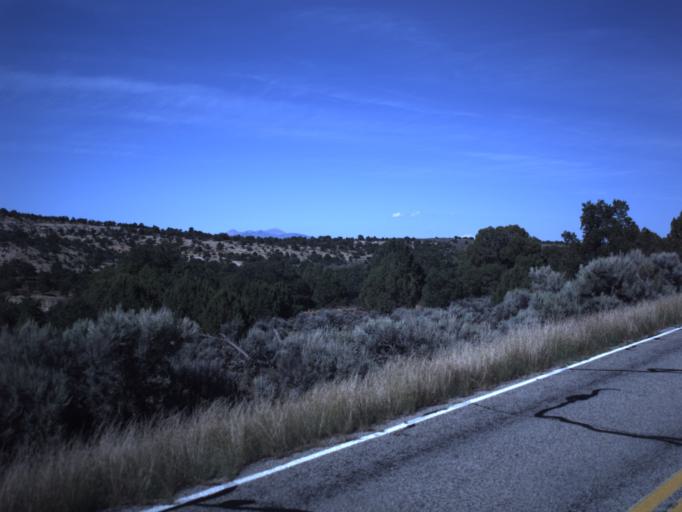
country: US
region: Utah
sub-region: San Juan County
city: Monticello
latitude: 37.9934
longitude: -109.4862
